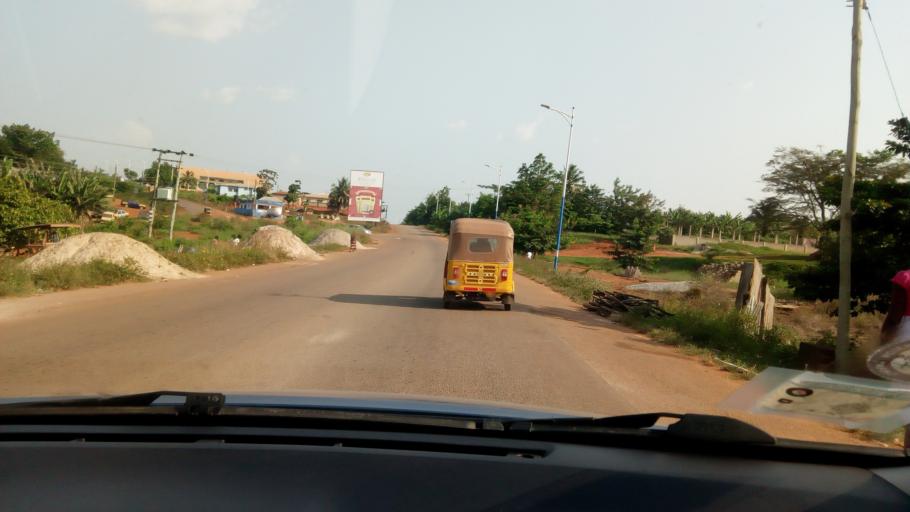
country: GH
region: Western
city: Bibiani
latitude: 6.8077
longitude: -2.5284
